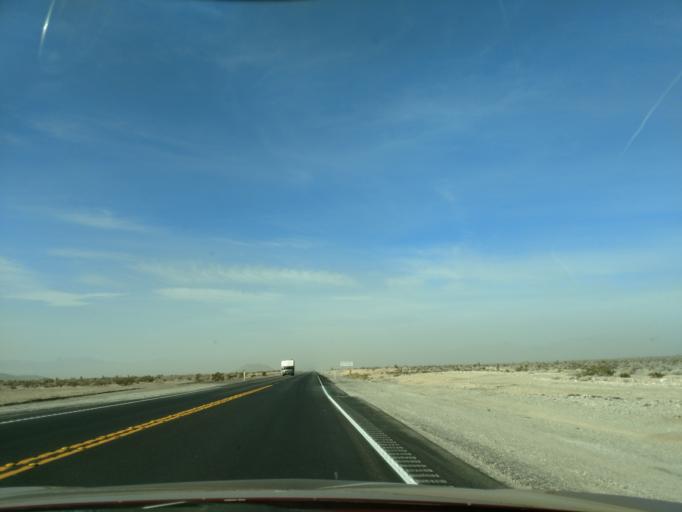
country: US
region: Nevada
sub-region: Nye County
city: Pahrump
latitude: 36.5654
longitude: -116.1274
